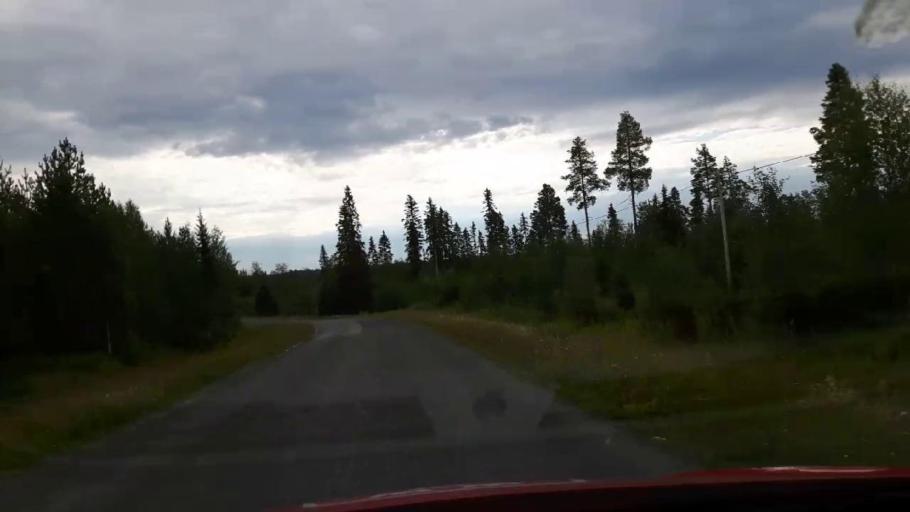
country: SE
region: Jaemtland
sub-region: OEstersunds Kommun
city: Lit
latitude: 63.3790
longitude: 15.0649
